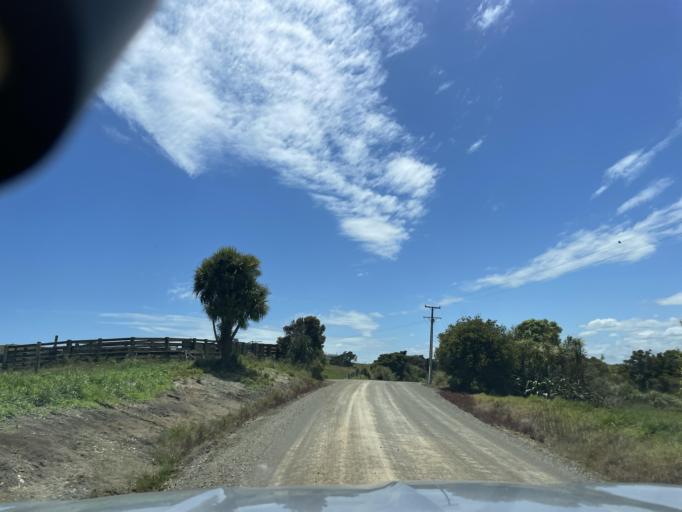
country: NZ
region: Auckland
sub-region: Auckland
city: Wellsford
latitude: -36.2224
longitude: 174.3622
